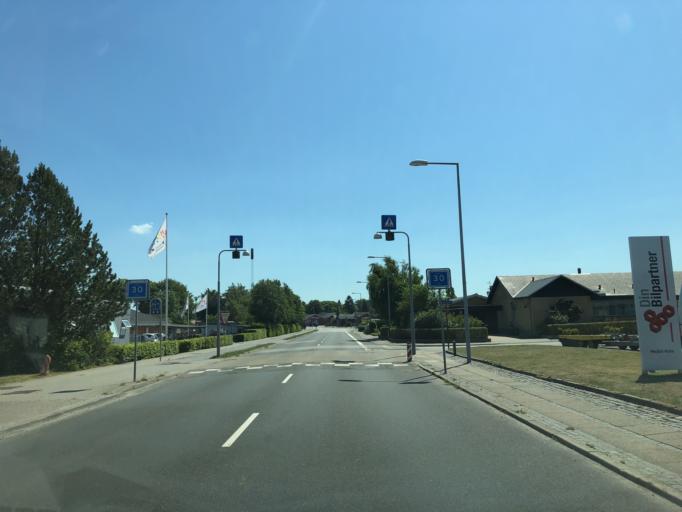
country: DK
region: Central Jutland
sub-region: Holstebro Kommune
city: Holstebro
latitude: 56.3481
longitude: 8.6418
